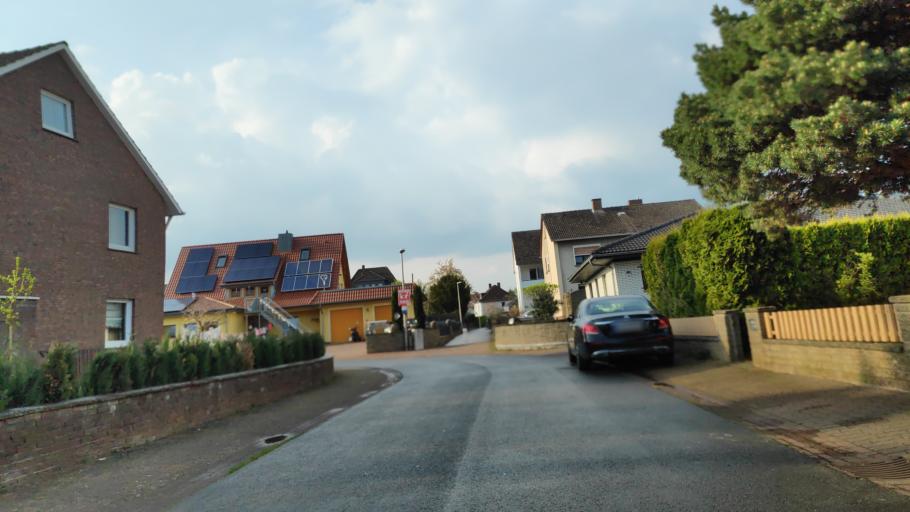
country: DE
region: North Rhine-Westphalia
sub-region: Regierungsbezirk Detmold
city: Minden
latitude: 52.2891
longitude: 8.9477
